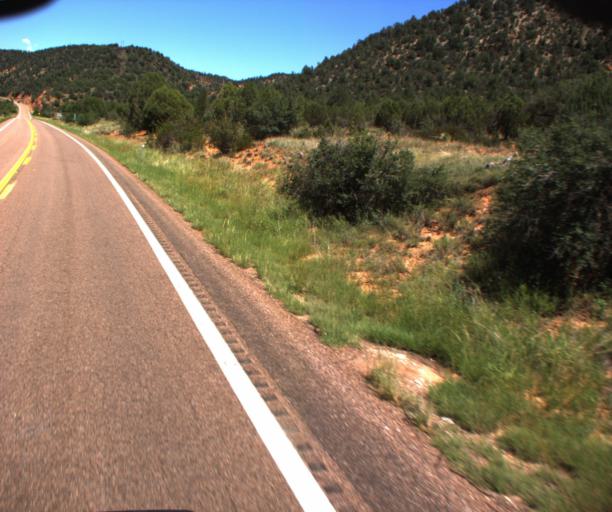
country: US
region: Arizona
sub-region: Navajo County
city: Cibecue
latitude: 34.0227
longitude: -110.2383
